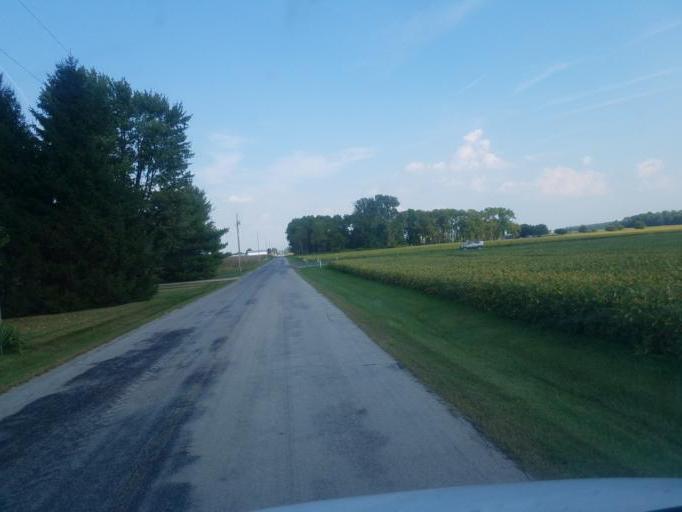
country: US
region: Ohio
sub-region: Wyandot County
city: Carey
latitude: 40.9050
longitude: -83.4634
